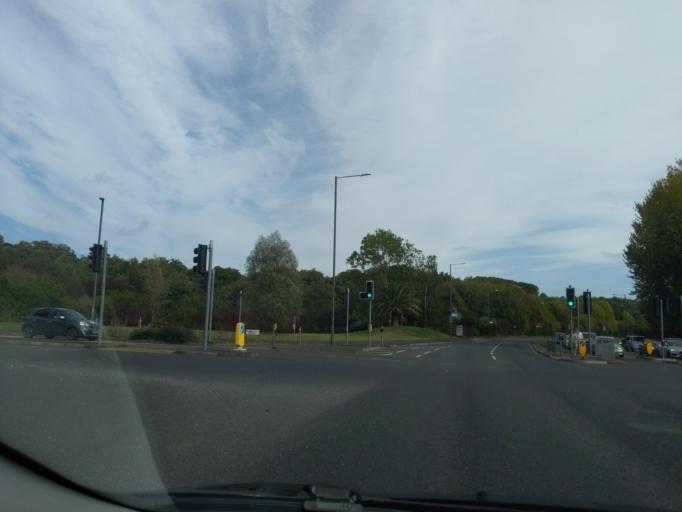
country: GB
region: England
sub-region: Devon
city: Kingskerswell
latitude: 50.4869
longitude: -3.5587
